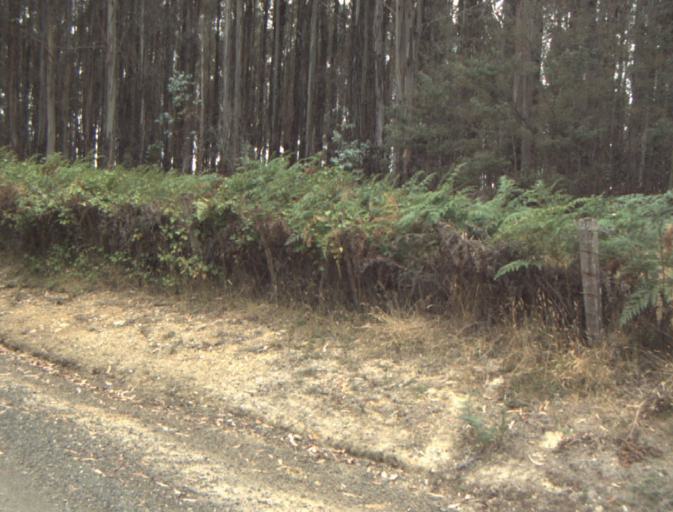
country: AU
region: Tasmania
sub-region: Launceston
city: Mayfield
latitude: -41.2136
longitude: 147.1779
